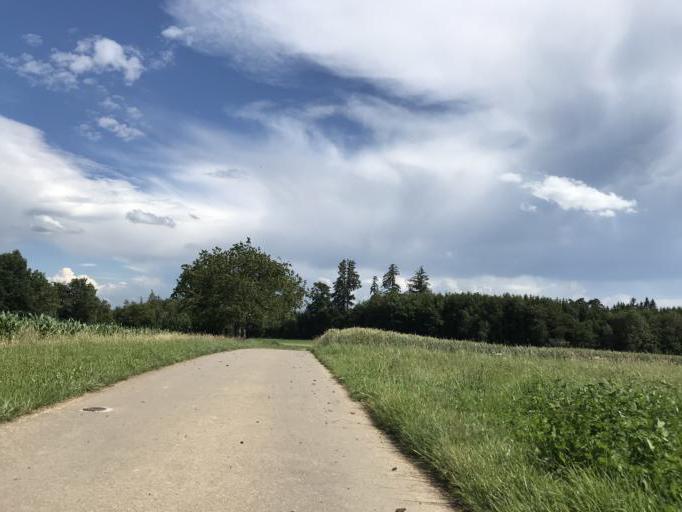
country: DE
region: Baden-Wuerttemberg
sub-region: Freiburg Region
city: Schopfheim
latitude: 47.6309
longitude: 7.8315
